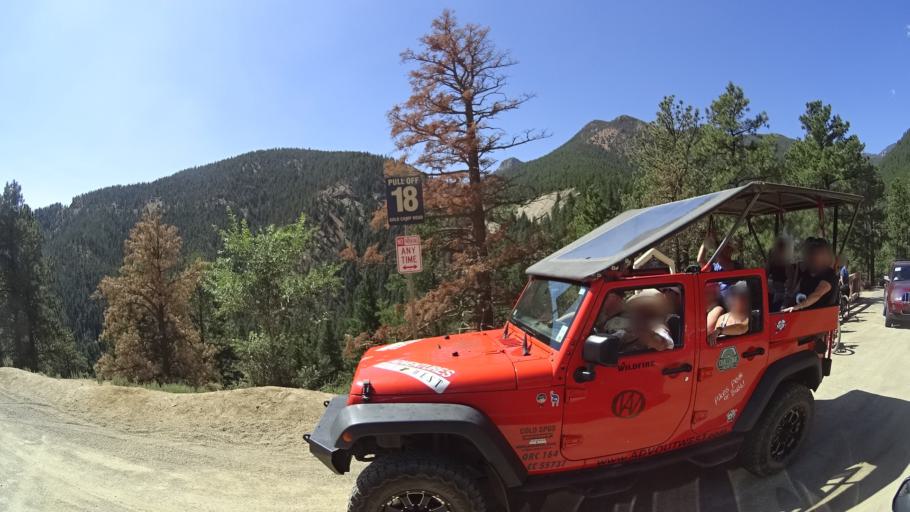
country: US
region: Colorado
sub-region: El Paso County
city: Manitou Springs
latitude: 38.7904
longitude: -104.9036
